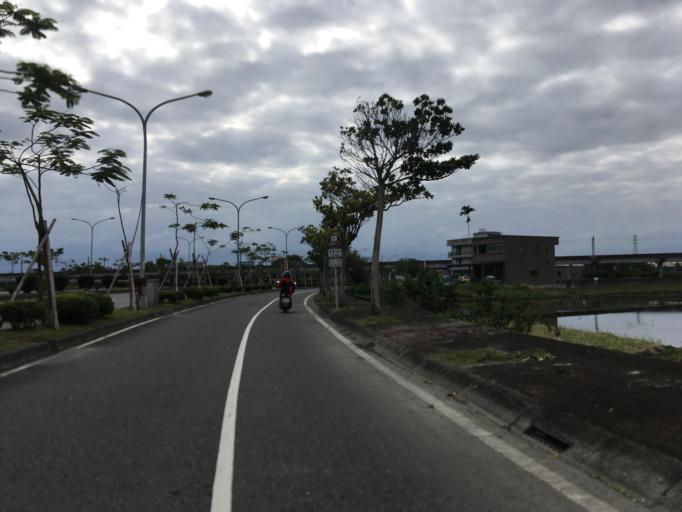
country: TW
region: Taiwan
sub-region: Yilan
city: Yilan
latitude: 24.7243
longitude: 121.7716
